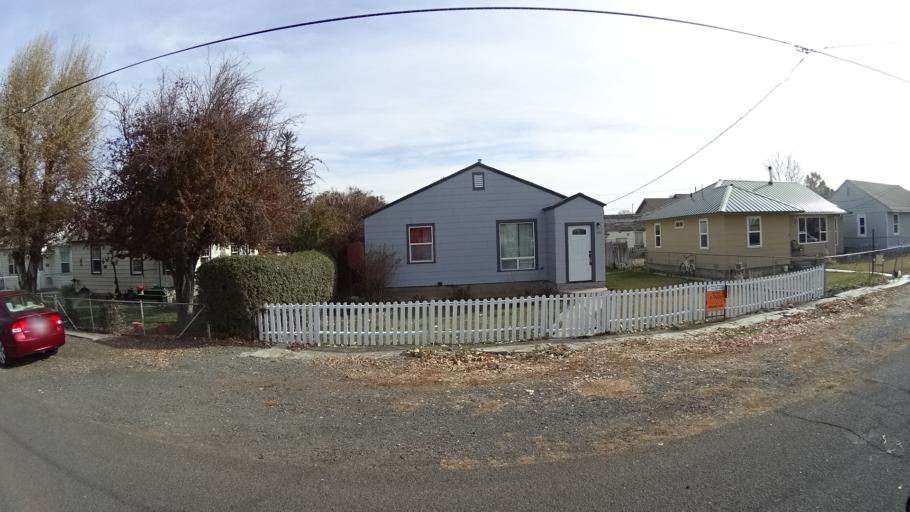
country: US
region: California
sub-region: Siskiyou County
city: Tulelake
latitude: 41.9579
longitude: -121.4791
